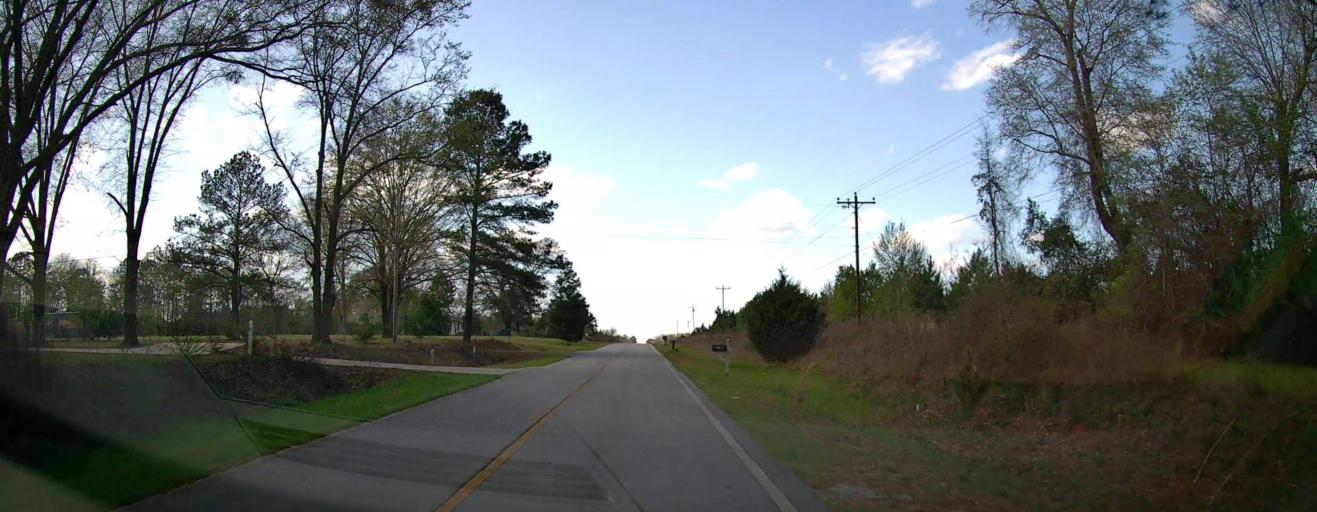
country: US
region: Georgia
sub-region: Wilkinson County
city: Gordon
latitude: 32.8293
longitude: -83.4272
